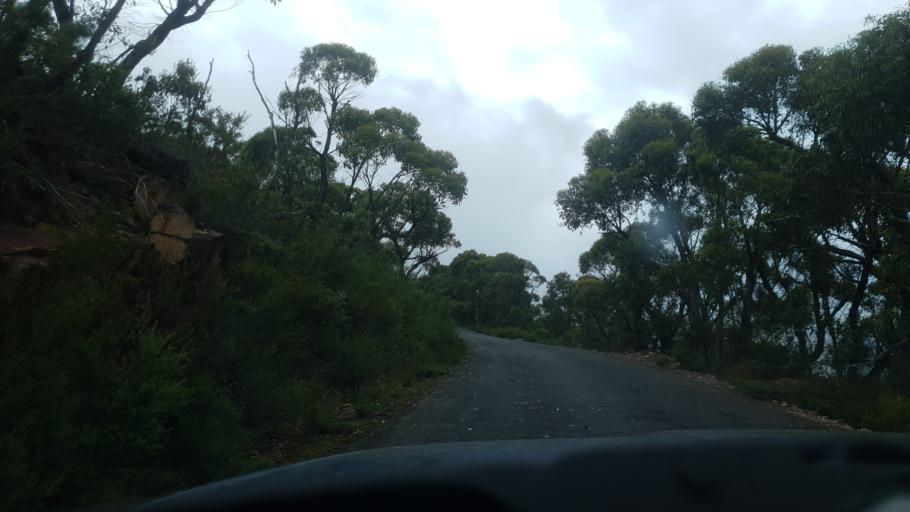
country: AU
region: Victoria
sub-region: Northern Grampians
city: Stawell
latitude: -37.2685
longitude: 142.5778
